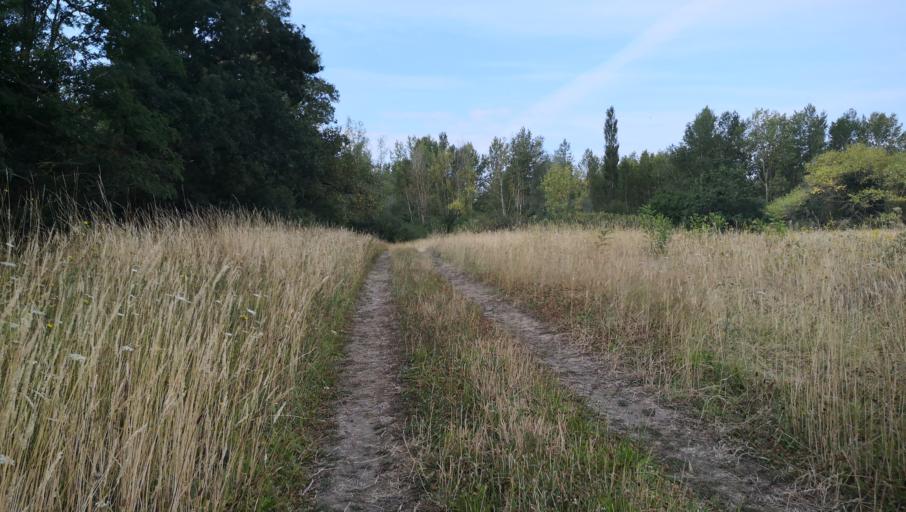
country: FR
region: Centre
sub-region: Departement du Loiret
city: Checy
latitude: 47.8931
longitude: 2.0036
